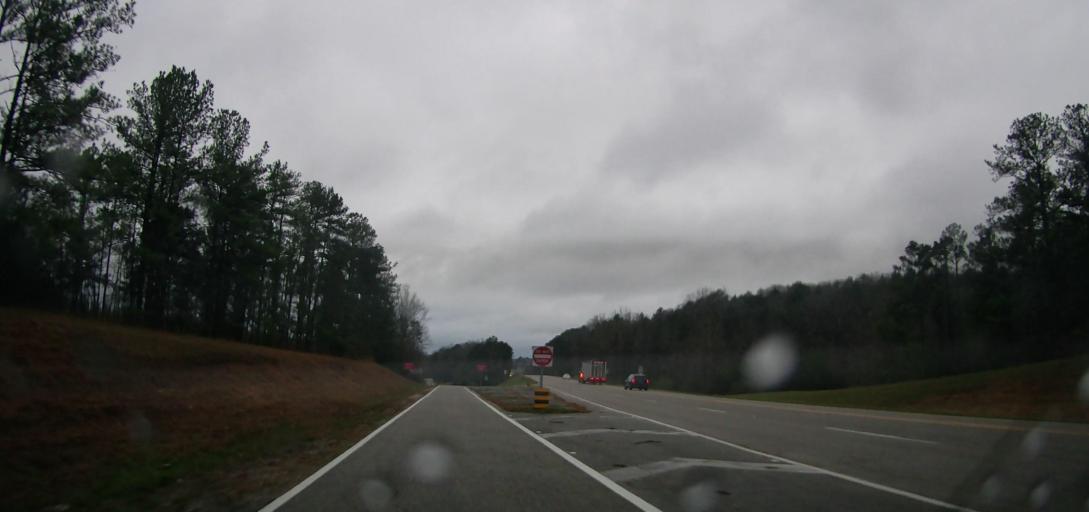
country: US
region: Alabama
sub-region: Bibb County
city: Centreville
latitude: 33.0304
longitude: -87.1424
